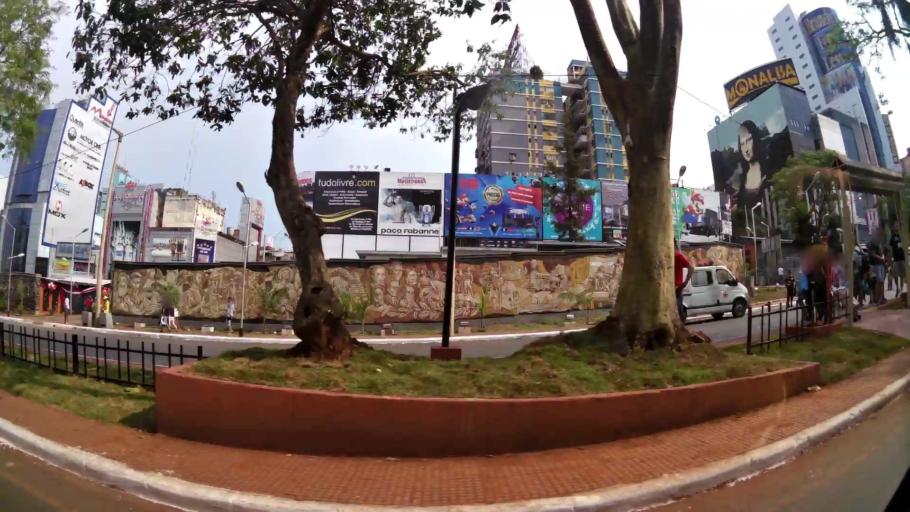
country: PY
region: Alto Parana
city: Ciudad del Este
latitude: -25.5092
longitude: -54.6096
